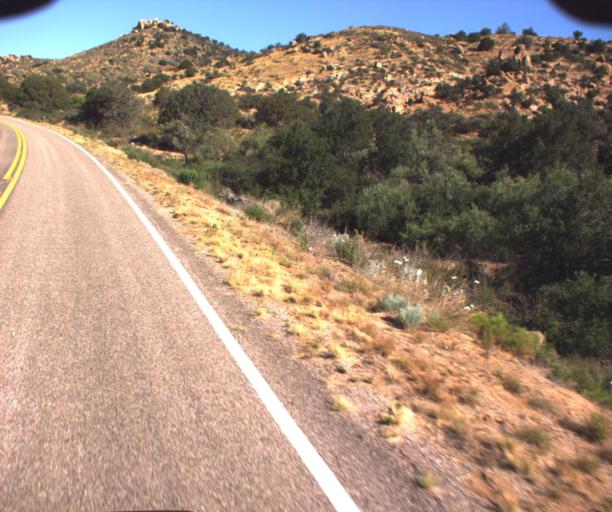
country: US
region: Arizona
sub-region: Graham County
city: Swift Trail Junction
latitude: 32.5741
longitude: -109.8345
